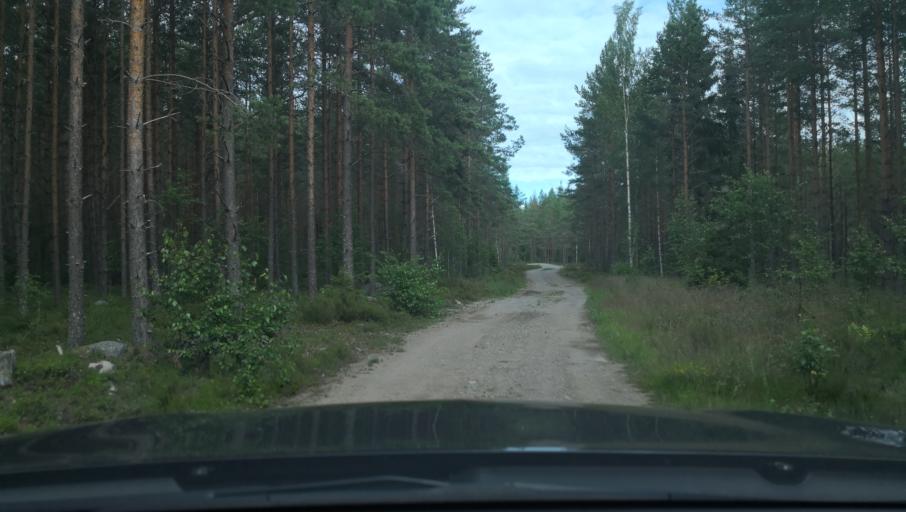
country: SE
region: Vaestmanland
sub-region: Surahammars Kommun
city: Surahammar
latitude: 59.6742
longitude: 16.1115
